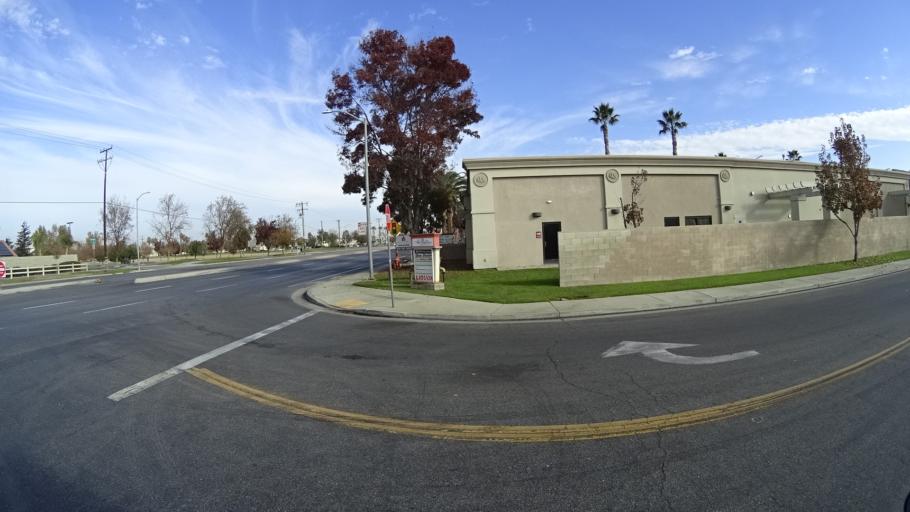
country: US
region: California
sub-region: Kern County
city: Greenacres
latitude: 35.3978
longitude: -119.1127
